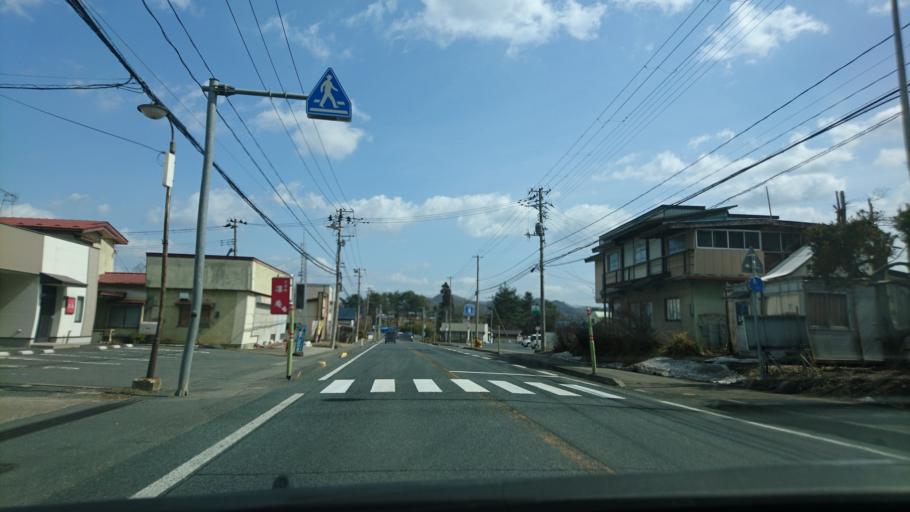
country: JP
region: Iwate
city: Shizukuishi
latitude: 39.6918
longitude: 141.0105
